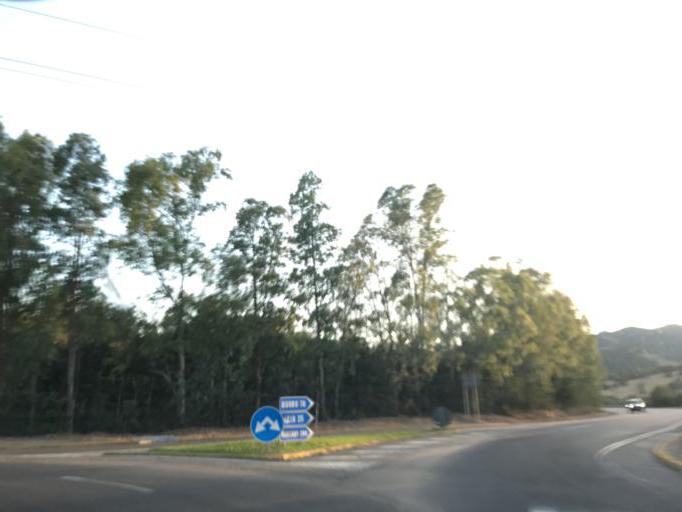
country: IT
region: Sardinia
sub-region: Provincia di Olbia-Tempio
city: San Teodoro
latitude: 40.7608
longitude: 9.6534
